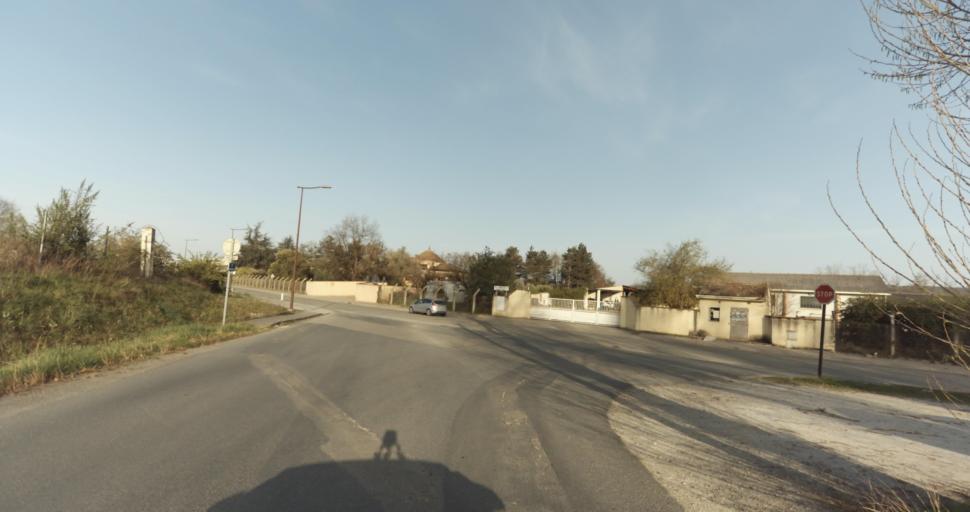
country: FR
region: Midi-Pyrenees
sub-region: Departement du Tarn
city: Saint-Sulpice-la-Pointe
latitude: 43.7673
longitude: 1.6665
